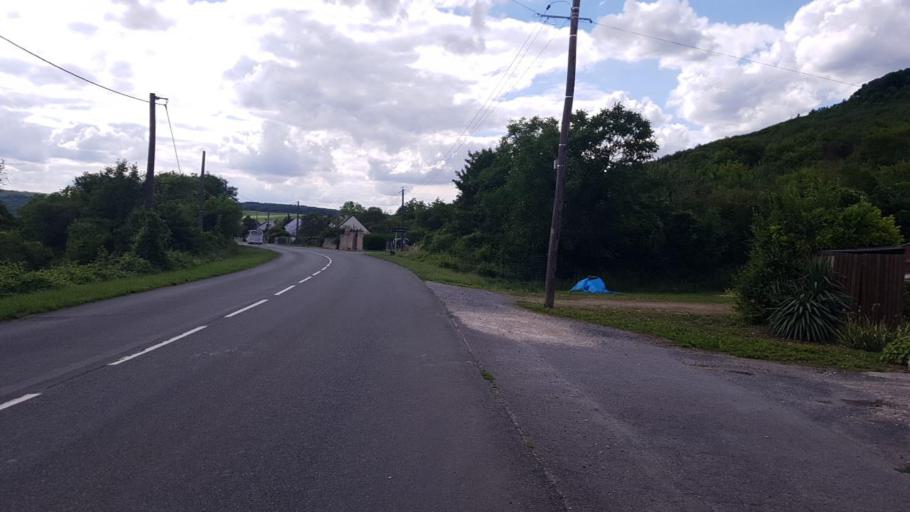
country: FR
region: Picardie
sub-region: Departement de l'Aisne
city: Crezancy
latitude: 49.0743
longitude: 3.5141
